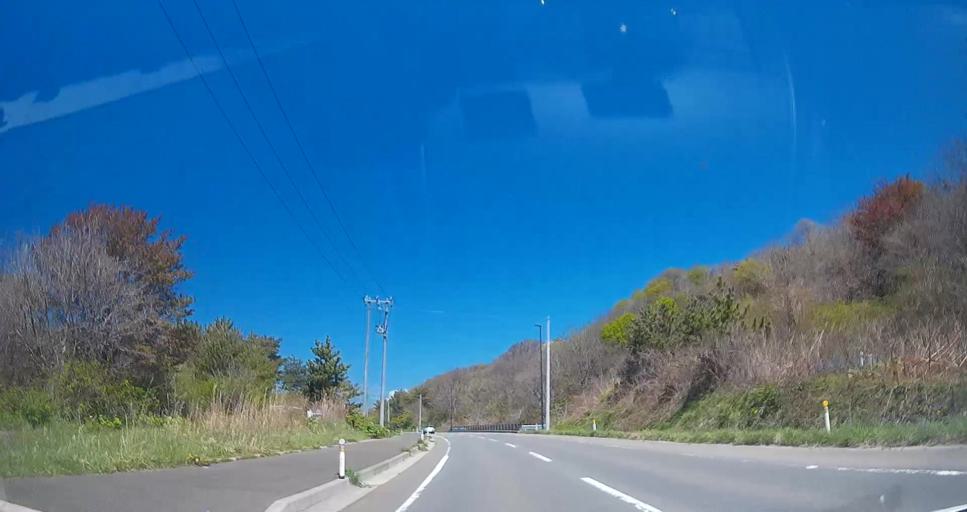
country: JP
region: Aomori
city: Mutsu
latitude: 41.3945
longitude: 141.4212
